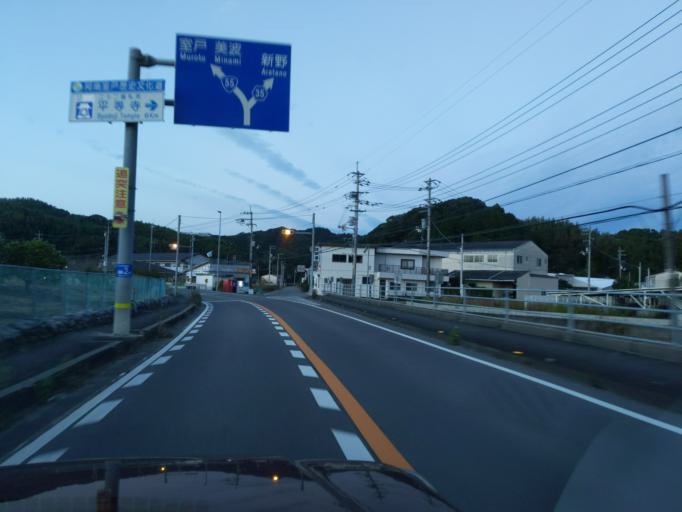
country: JP
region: Tokushima
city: Anan
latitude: 33.8605
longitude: 134.6278
